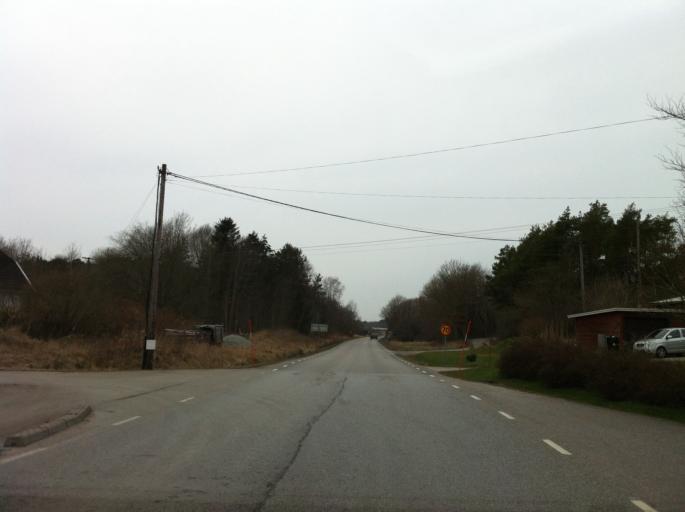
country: SE
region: Vaestra Goetaland
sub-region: Orust
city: Henan
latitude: 58.1873
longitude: 11.6924
